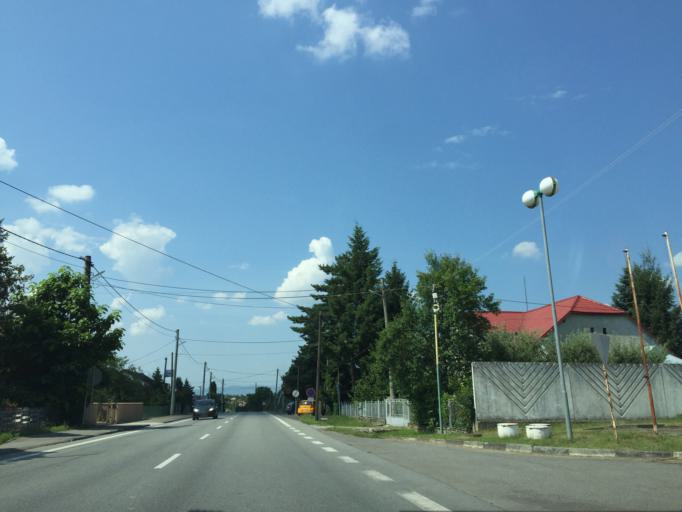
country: UA
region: Zakarpattia
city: Storozhnytsya
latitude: 48.6760
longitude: 22.2513
